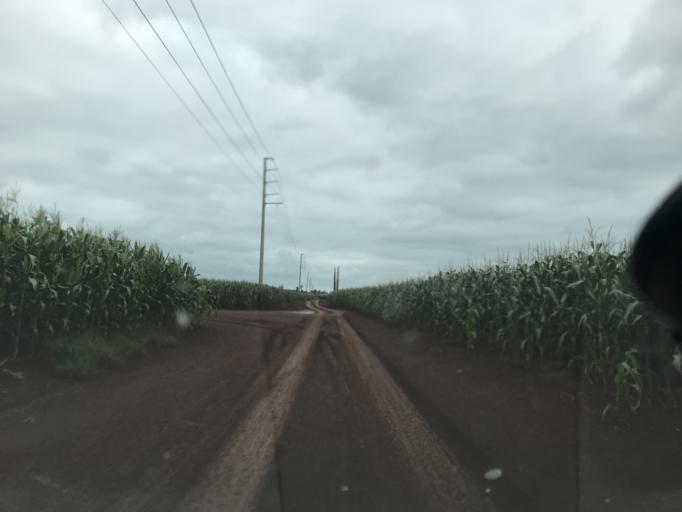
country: BR
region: Parana
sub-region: Palotina
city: Palotina
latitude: -24.3051
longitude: -53.8218
